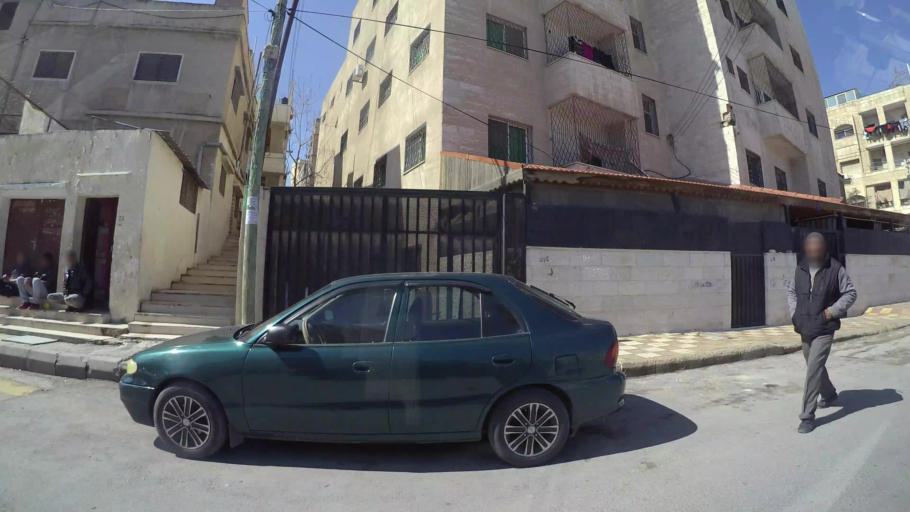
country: JO
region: Amman
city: Amman
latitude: 31.9825
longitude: 35.9819
